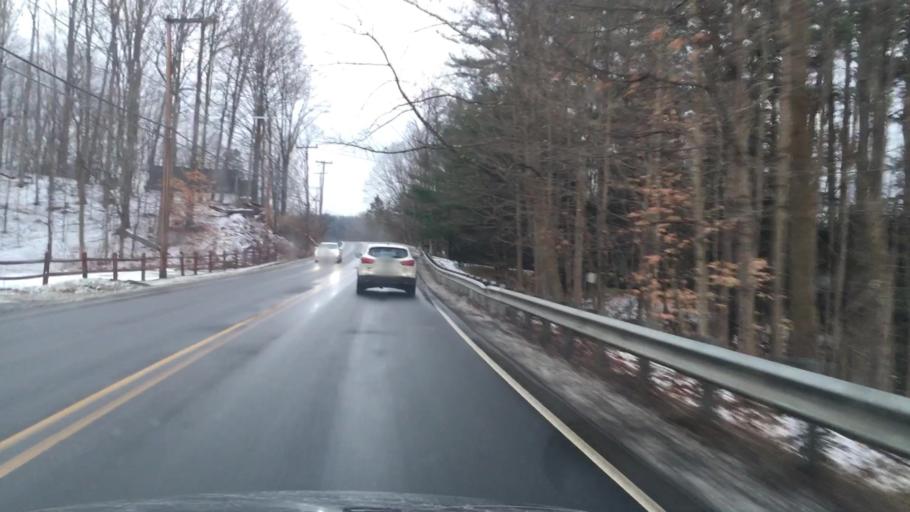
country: US
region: New Hampshire
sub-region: Sullivan County
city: Claremont
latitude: 43.3919
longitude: -72.3674
